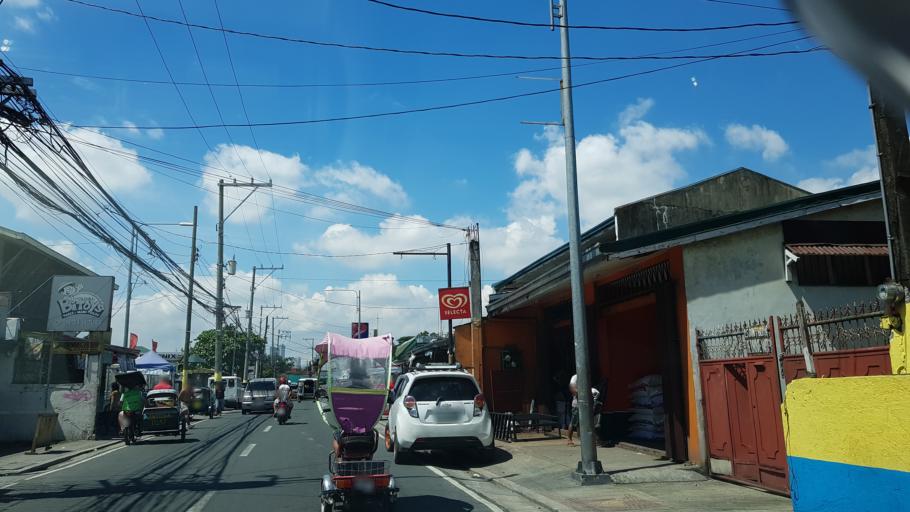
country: PH
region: Calabarzon
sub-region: Province of Rizal
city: Pateros
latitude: 14.5385
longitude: 121.0675
